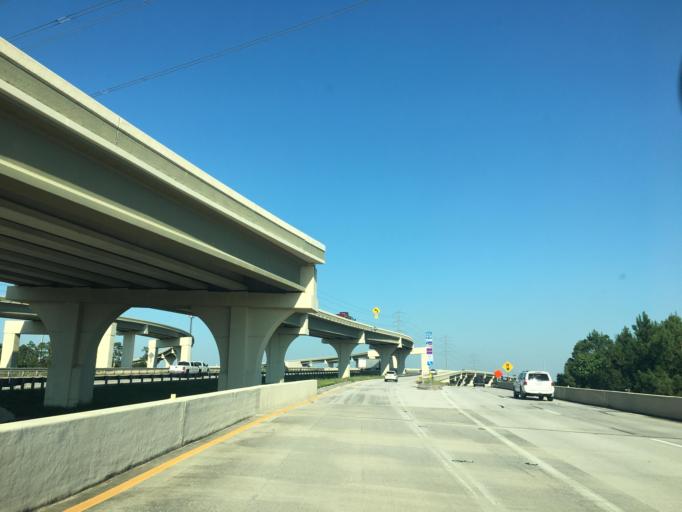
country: US
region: Texas
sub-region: Harris County
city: Spring
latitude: 30.0919
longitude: -95.4391
